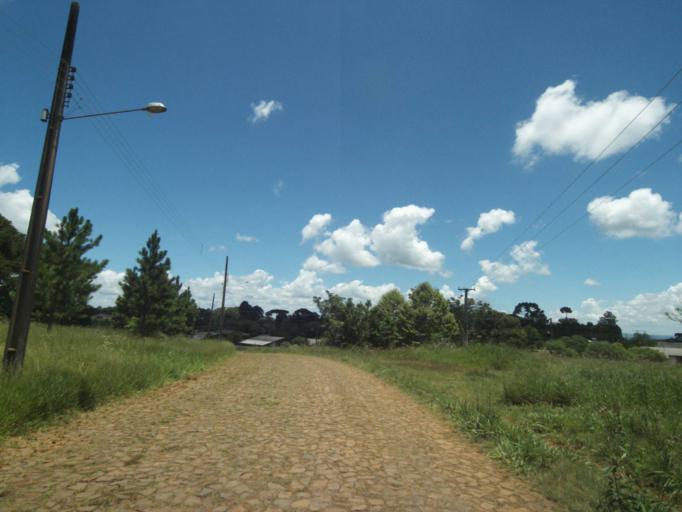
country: BR
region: Parana
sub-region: Pinhao
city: Pinhao
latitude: -25.7902
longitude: -52.0816
